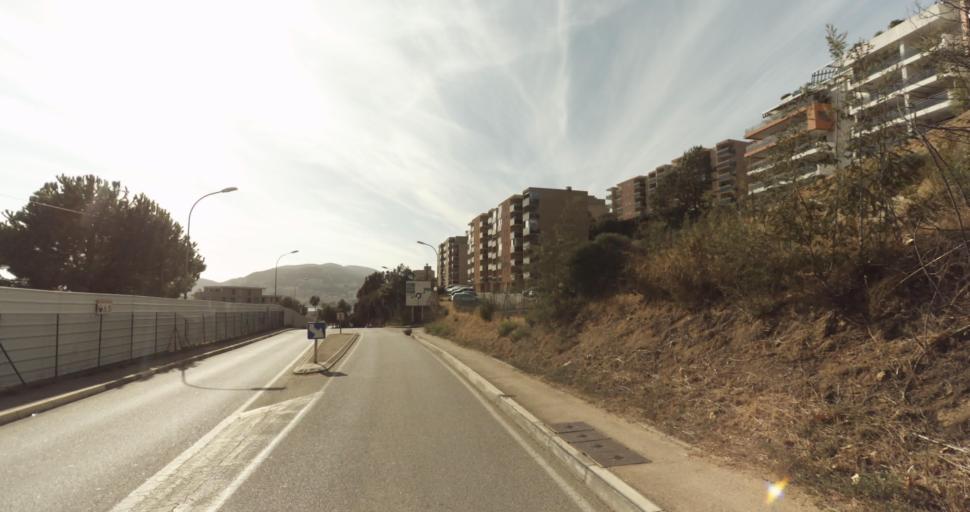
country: FR
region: Corsica
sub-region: Departement de la Corse-du-Sud
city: Ajaccio
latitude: 41.9301
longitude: 8.7629
